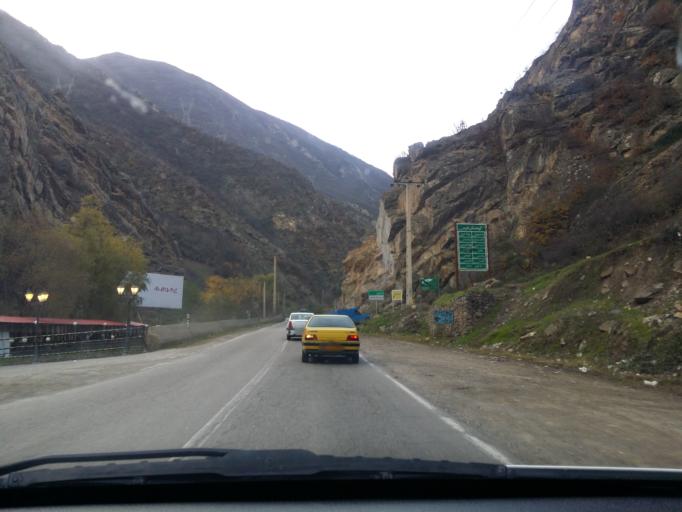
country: IR
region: Mazandaran
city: Chalus
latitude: 36.3139
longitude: 51.2478
